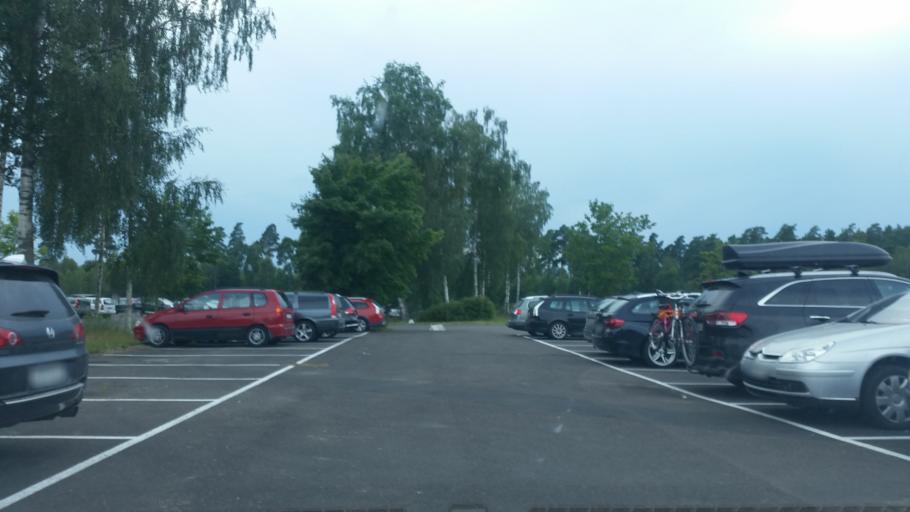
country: SE
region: Vaestra Goetaland
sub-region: Skara Kommun
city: Axvall
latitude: 58.4024
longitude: 13.5492
